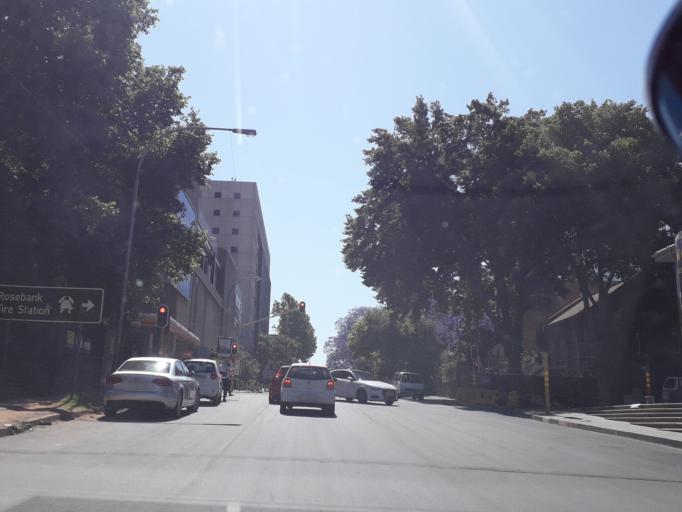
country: ZA
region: Gauteng
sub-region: City of Johannesburg Metropolitan Municipality
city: Johannesburg
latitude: -26.1480
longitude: 28.0405
